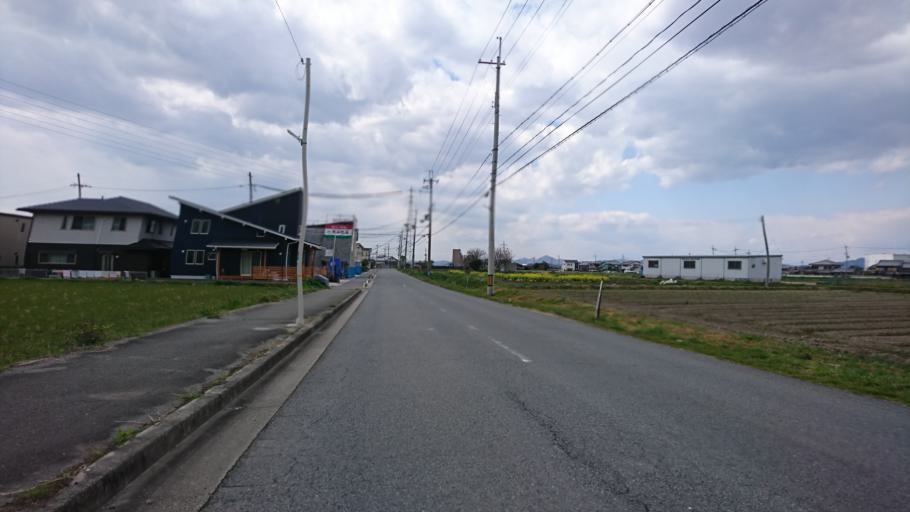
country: JP
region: Hyogo
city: Miki
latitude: 34.7534
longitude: 134.9177
